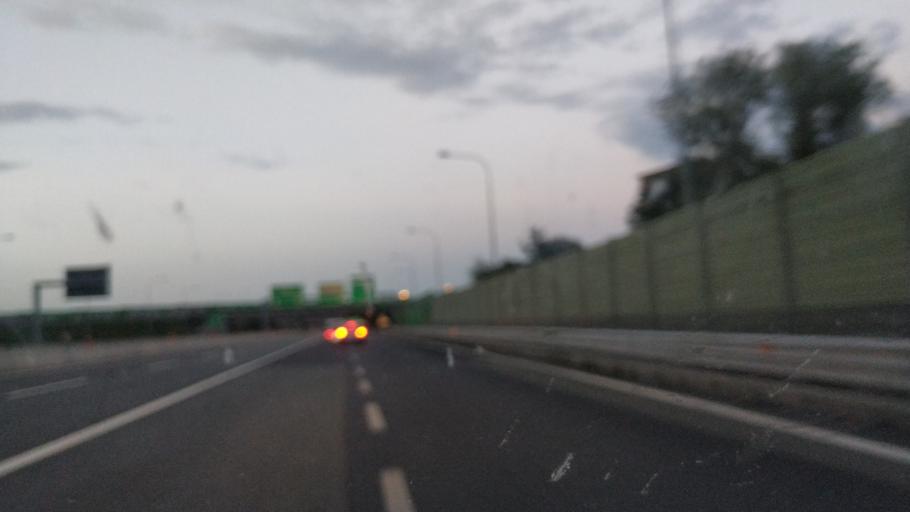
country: IT
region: Piedmont
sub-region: Provincia di Torino
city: Leini
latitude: 45.1326
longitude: 7.7076
